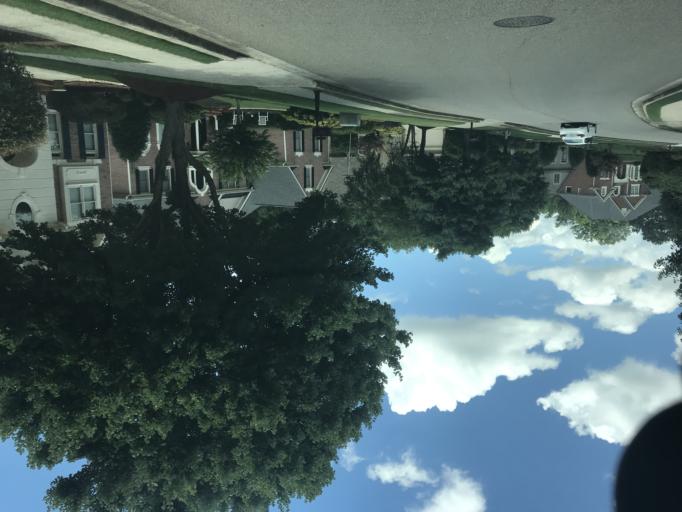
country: US
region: Georgia
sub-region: Fulton County
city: Johns Creek
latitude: 34.0795
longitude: -84.1736
